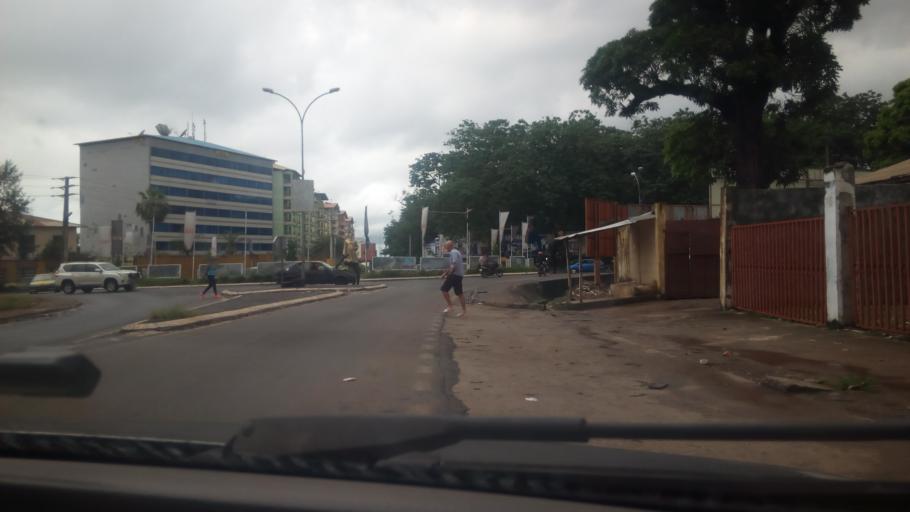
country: GN
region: Conakry
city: Camayenne
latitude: 9.5249
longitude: -13.6861
